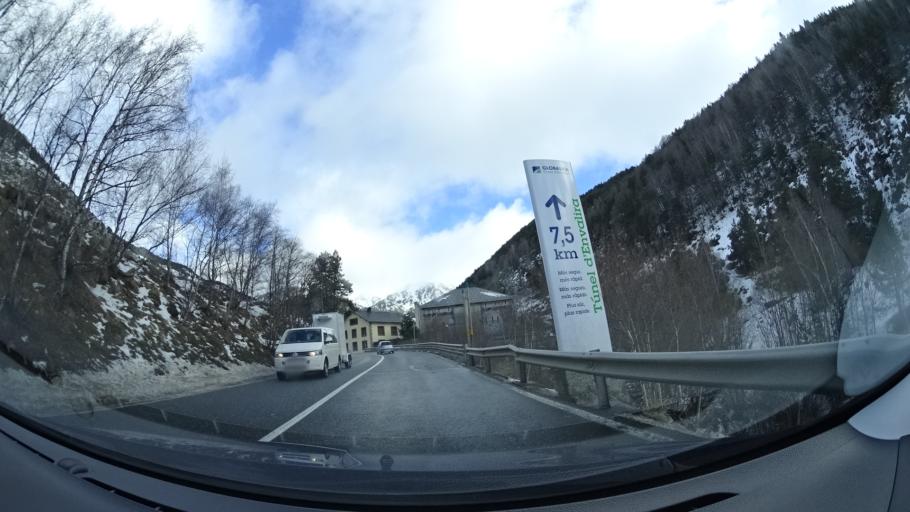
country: AD
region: Canillo
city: El Tarter
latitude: 42.5789
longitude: 1.6378
